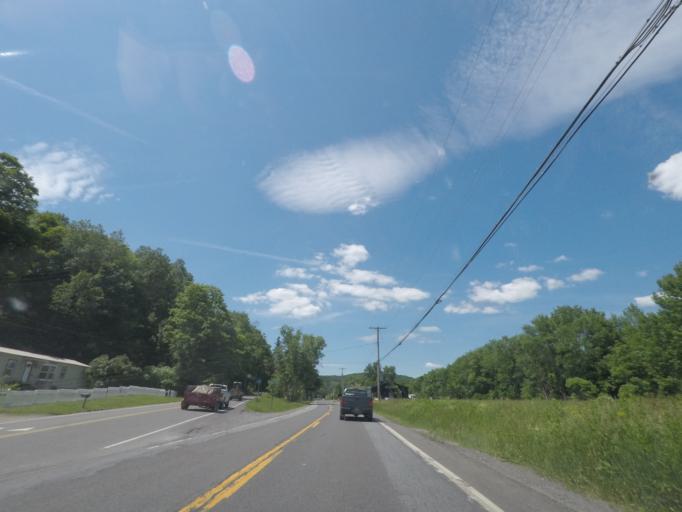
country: US
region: New York
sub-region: Dutchess County
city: Pine Plains
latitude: 41.9608
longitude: -73.5191
